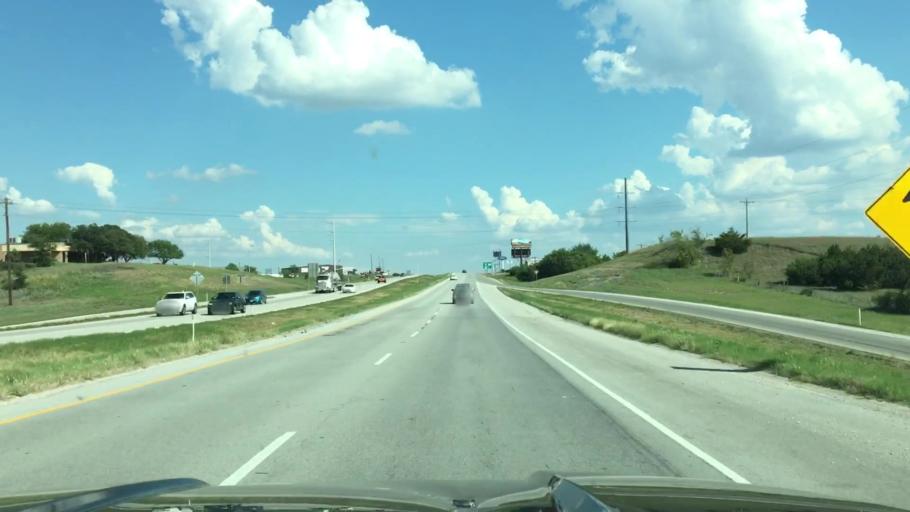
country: US
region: Texas
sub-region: Wise County
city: Decatur
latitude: 33.2136
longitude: -97.5821
